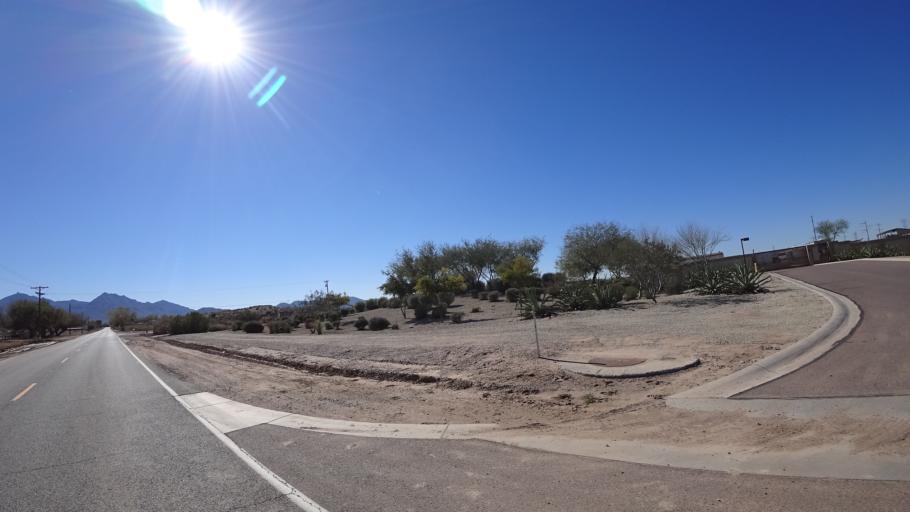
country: US
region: Arizona
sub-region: Maricopa County
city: Avondale
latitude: 33.3999
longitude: -112.3405
